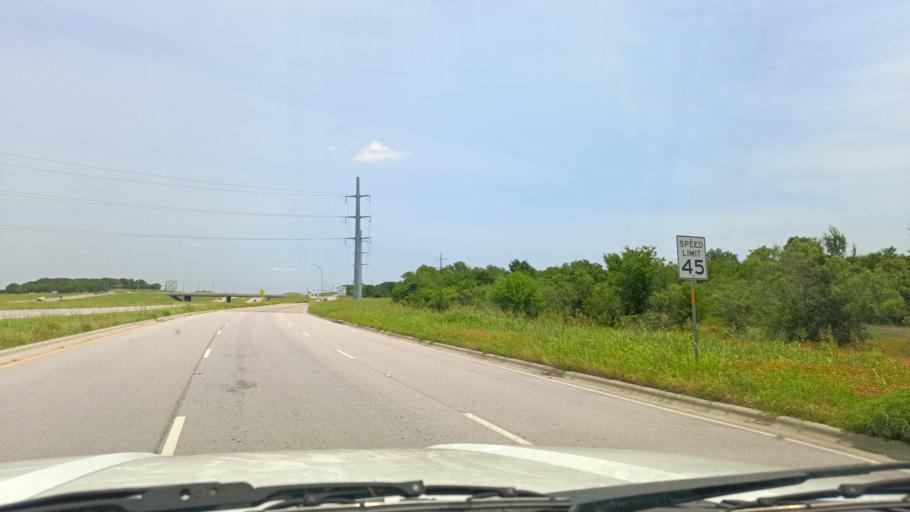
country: US
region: Texas
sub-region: Bell County
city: Temple
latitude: 31.1143
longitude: -97.3879
